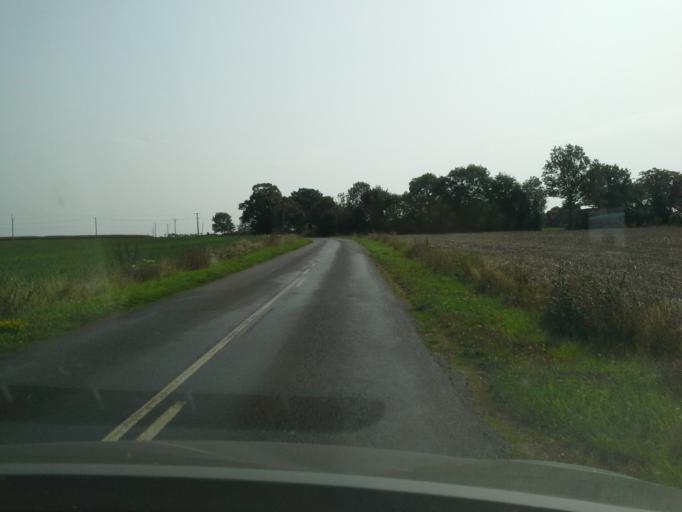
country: FR
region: Centre
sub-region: Departement du Loir-et-Cher
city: La Ville-aux-Clercs
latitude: 47.9087
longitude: 1.0610
